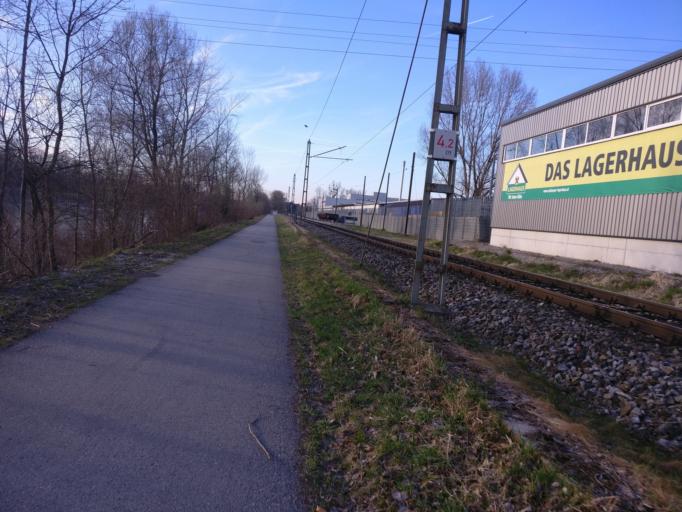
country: AT
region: Salzburg
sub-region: Politischer Bezirk Salzburg-Umgebung
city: Bergheim
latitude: 47.8437
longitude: 13.0151
